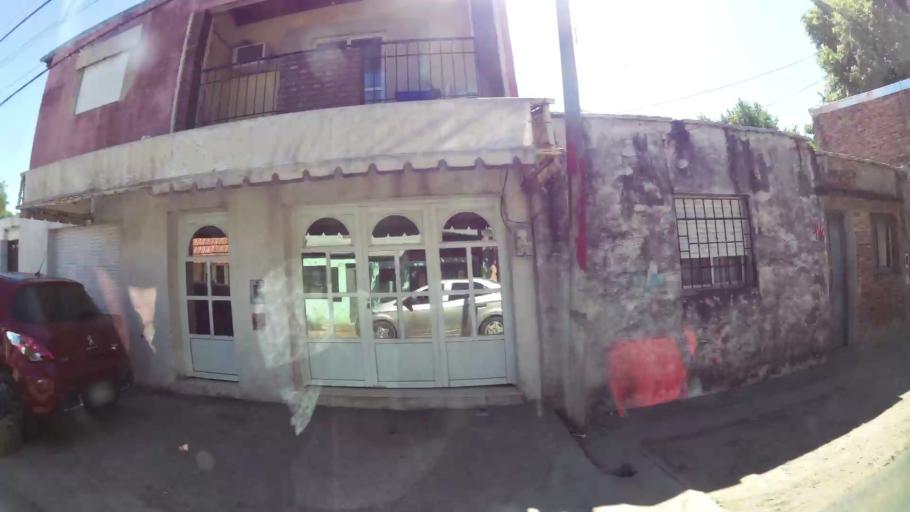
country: AR
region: Santa Fe
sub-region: Departamento de Rosario
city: Rosario
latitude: -32.9332
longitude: -60.6920
